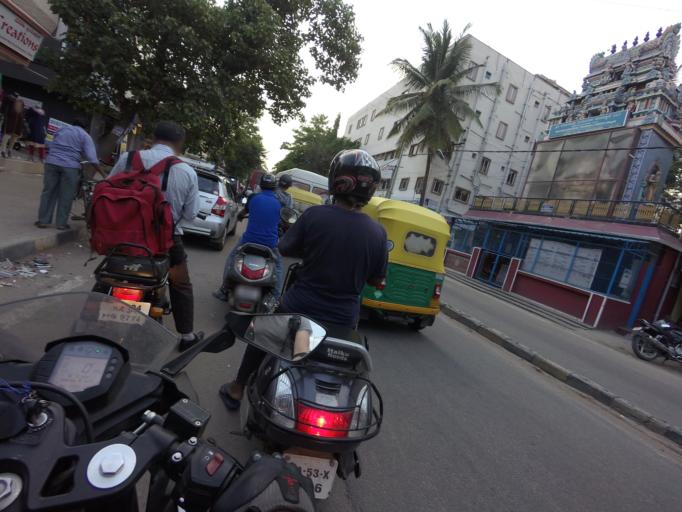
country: IN
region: Karnataka
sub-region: Bangalore Urban
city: Bangalore
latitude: 13.0152
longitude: 77.6360
